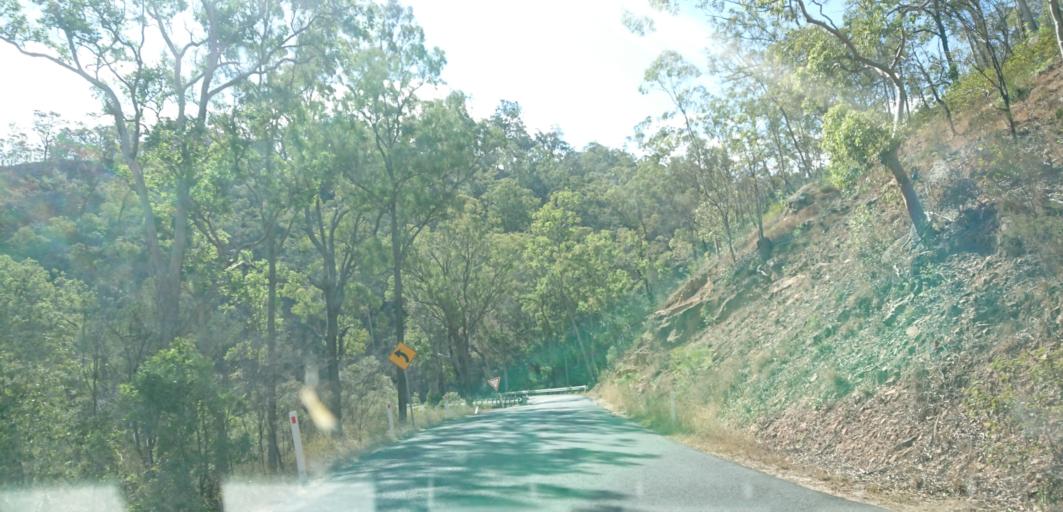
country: AU
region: Queensland
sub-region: Toowoomba
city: Top Camp
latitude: -27.7684
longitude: 152.0889
